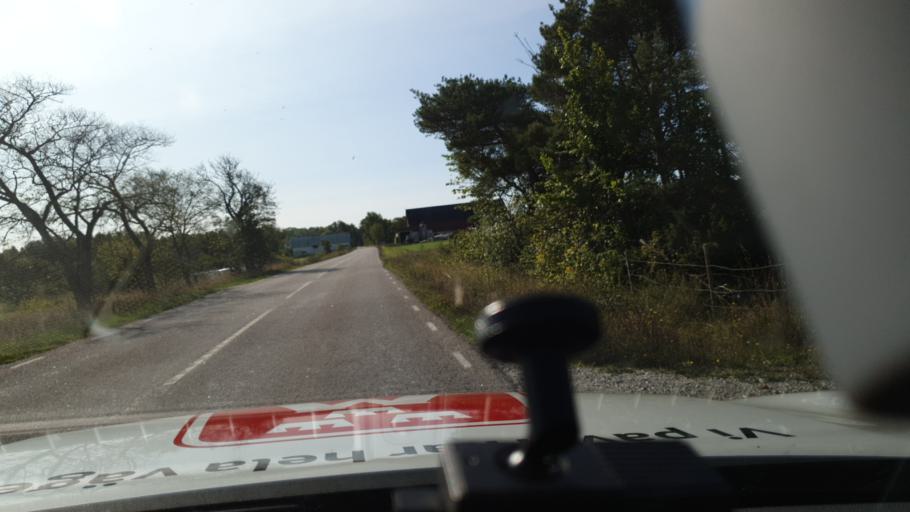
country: SE
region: Gotland
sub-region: Gotland
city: Hemse
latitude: 57.0994
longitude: 18.3035
